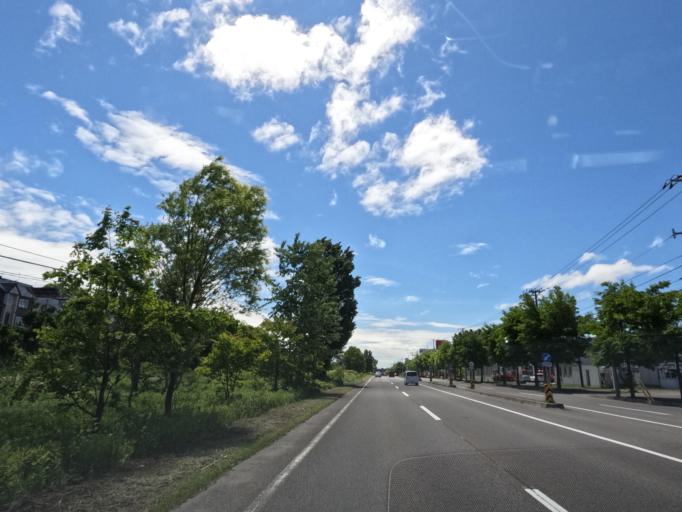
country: JP
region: Hokkaido
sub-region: Asahikawa-shi
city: Asahikawa
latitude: 43.7335
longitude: 142.3640
